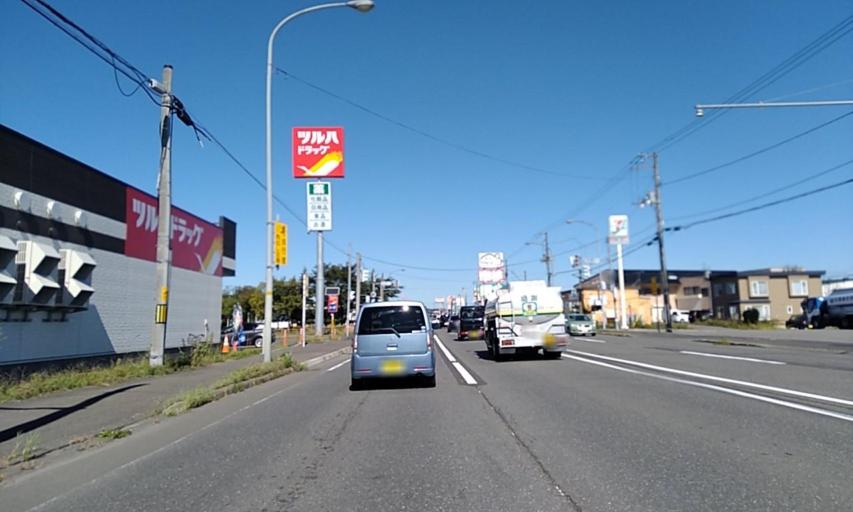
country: JP
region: Hokkaido
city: Kitahiroshima
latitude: 42.8885
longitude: 141.5698
